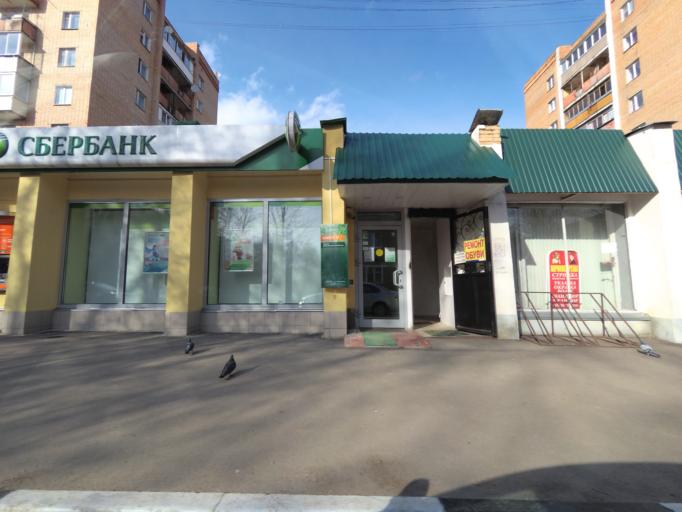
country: RU
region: Moskovskaya
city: Lugovaya
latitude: 56.0464
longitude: 37.4848
